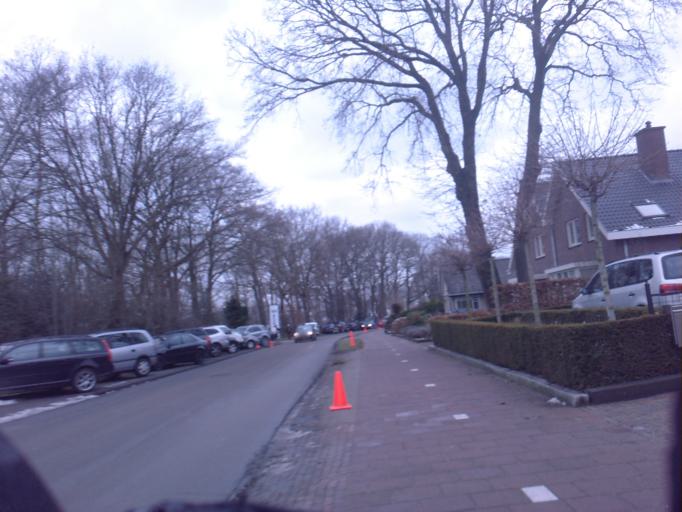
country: NL
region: Gelderland
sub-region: Gemeente Barneveld
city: Terschuur
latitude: 52.1380
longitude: 5.4904
